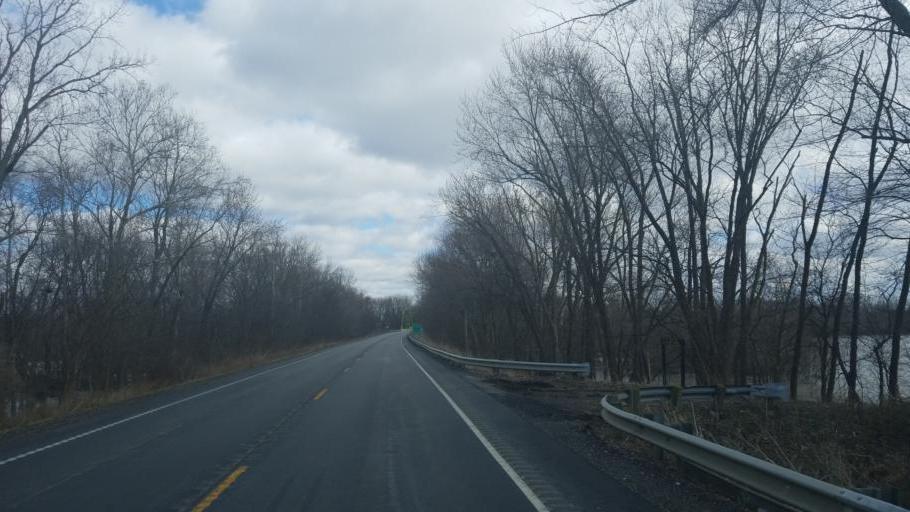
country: US
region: Indiana
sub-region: Parke County
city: Montezuma
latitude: 39.7914
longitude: -87.3823
